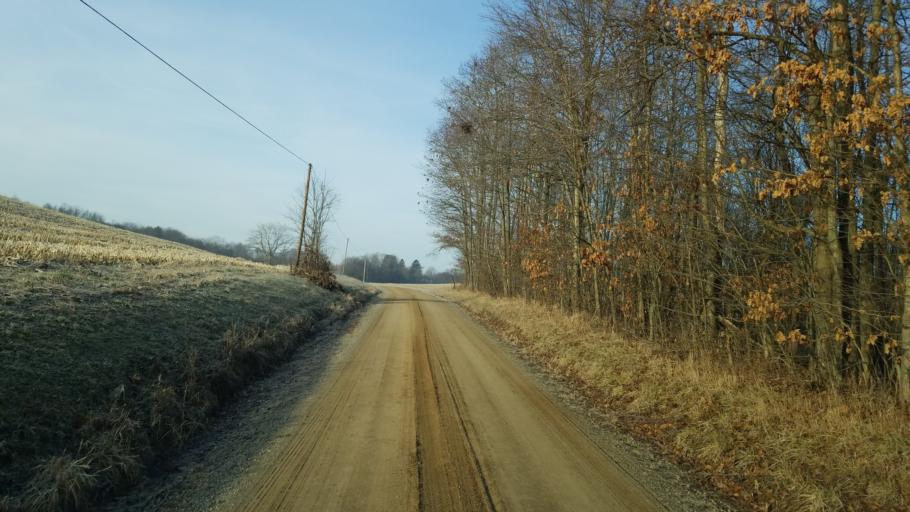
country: US
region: Pennsylvania
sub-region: Indiana County
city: Chevy Chase Heights
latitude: 40.8464
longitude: -79.2500
